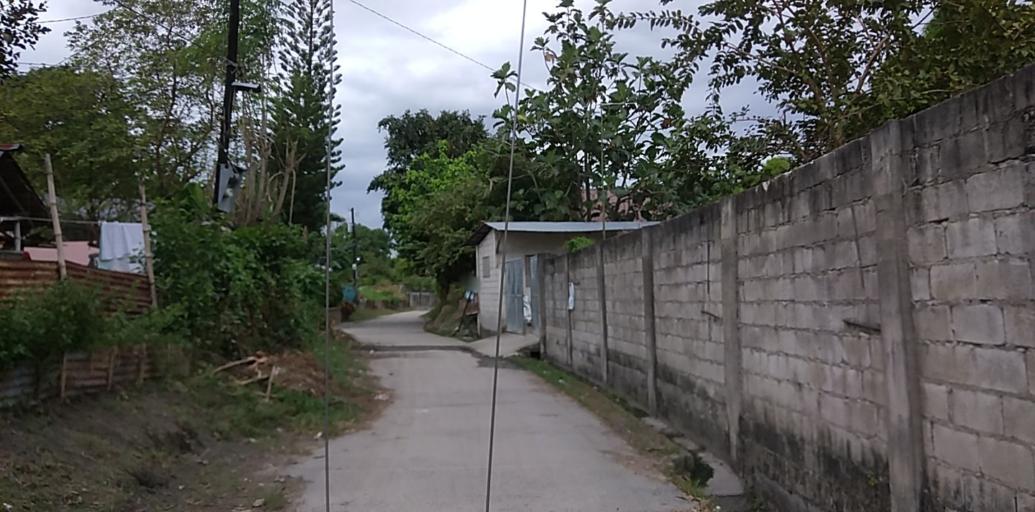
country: PH
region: Central Luzon
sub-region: Province of Pampanga
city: Pulung Santol
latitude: 15.0419
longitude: 120.5641
